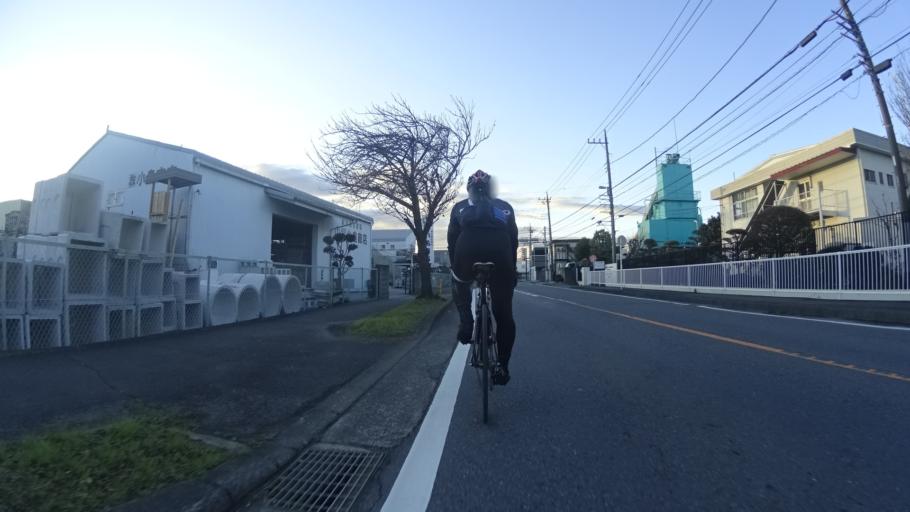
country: JP
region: Kanagawa
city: Atsugi
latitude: 35.4584
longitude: 139.3682
